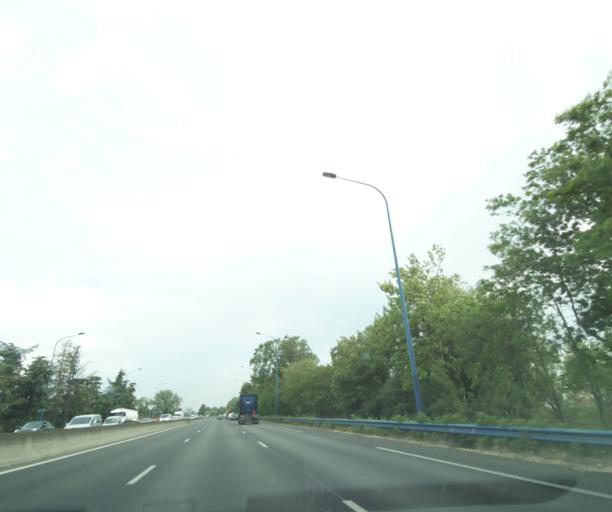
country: FR
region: Midi-Pyrenees
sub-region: Departement de la Haute-Garonne
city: Blagnac
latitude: 43.6374
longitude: 1.4214
